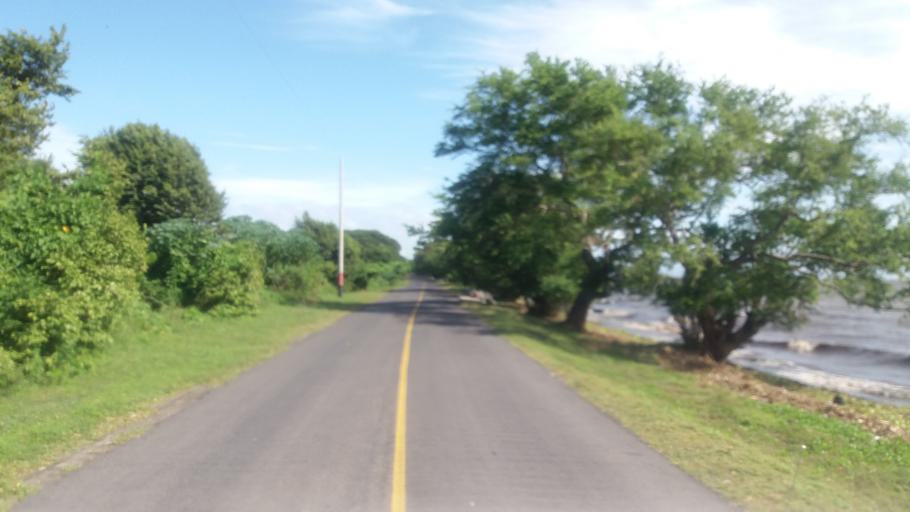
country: NI
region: Granada
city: Granada
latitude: 11.9748
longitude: -85.9424
